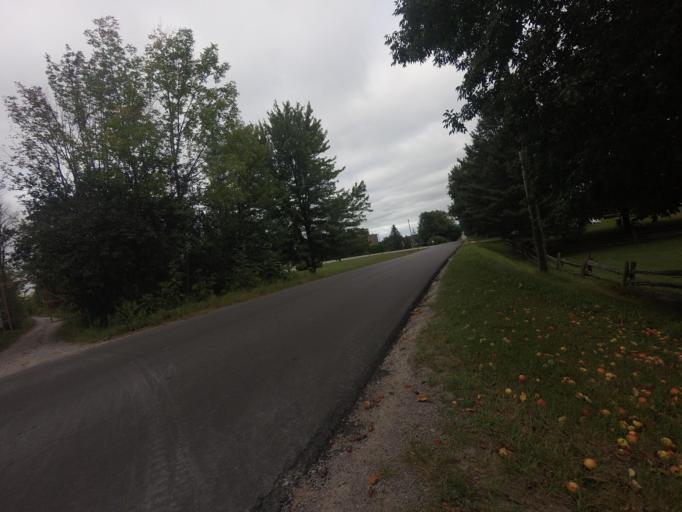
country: CA
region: Ontario
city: Omemee
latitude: 44.4293
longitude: -78.7691
